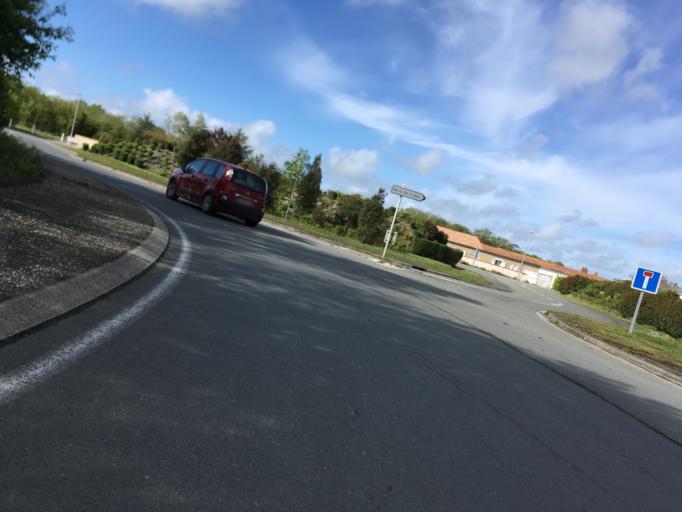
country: FR
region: Poitou-Charentes
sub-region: Departement de la Charente-Maritime
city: Dompierre-sur-Mer
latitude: 46.1747
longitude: -1.0650
